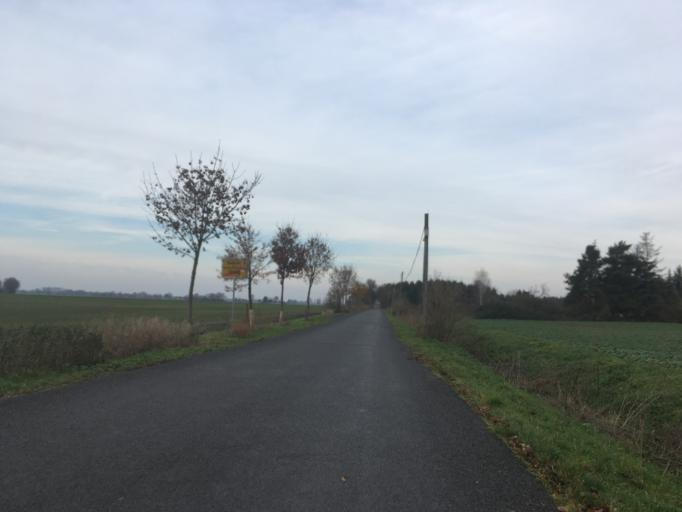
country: DE
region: Brandenburg
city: Letschin
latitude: 52.7057
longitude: 14.3498
